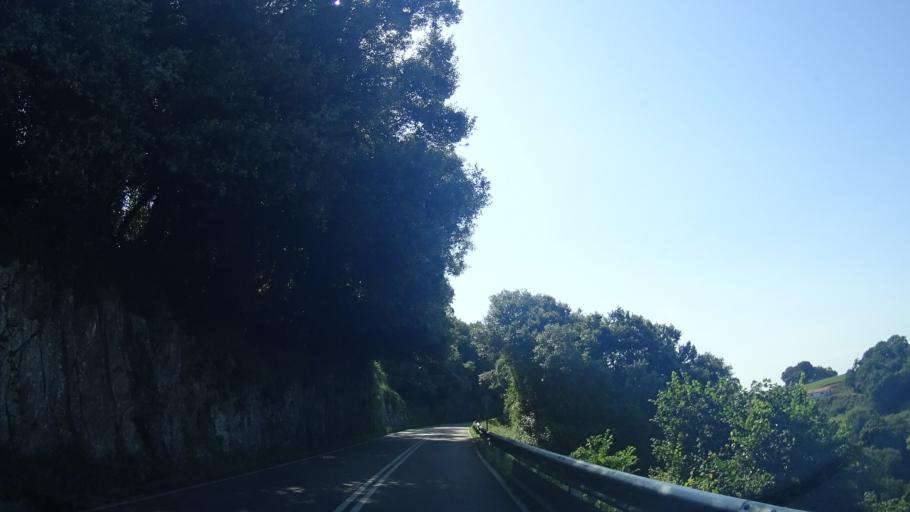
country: ES
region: Asturias
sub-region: Province of Asturias
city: Ribadesella
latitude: 43.4641
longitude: -5.1038
